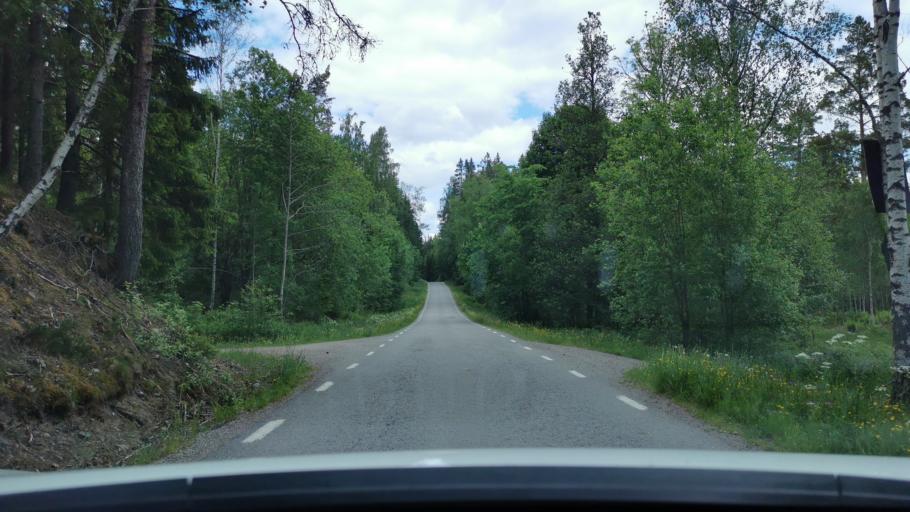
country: SE
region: Vaestra Goetaland
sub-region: Bengtsfors Kommun
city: Dals Langed
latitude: 58.8489
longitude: 12.3326
